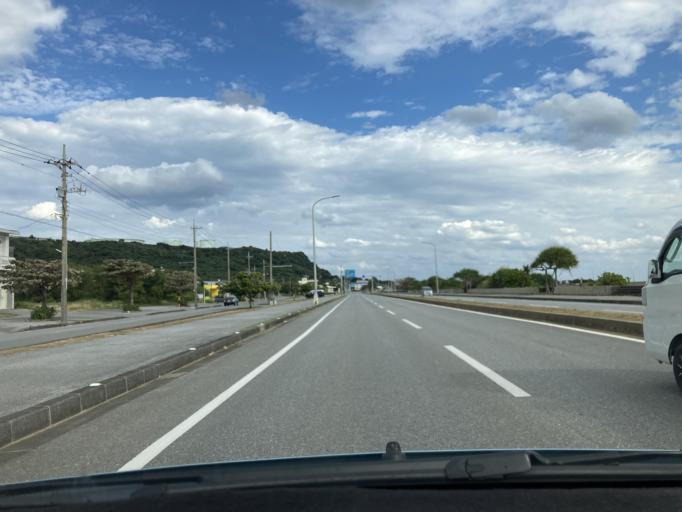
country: JP
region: Okinawa
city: Katsuren-haebaru
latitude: 26.3404
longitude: 127.9497
